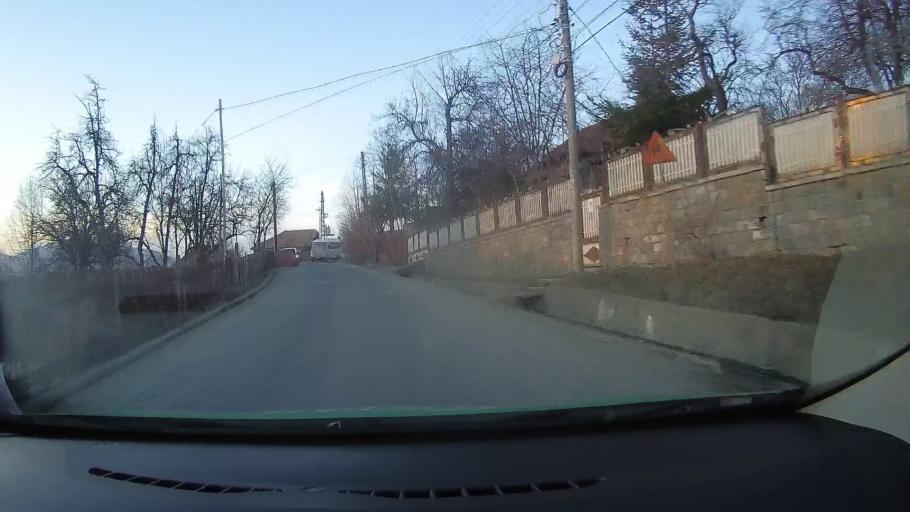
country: RO
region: Prahova
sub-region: Comuna Comarnic
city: Comarnic
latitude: 45.2517
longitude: 25.6433
